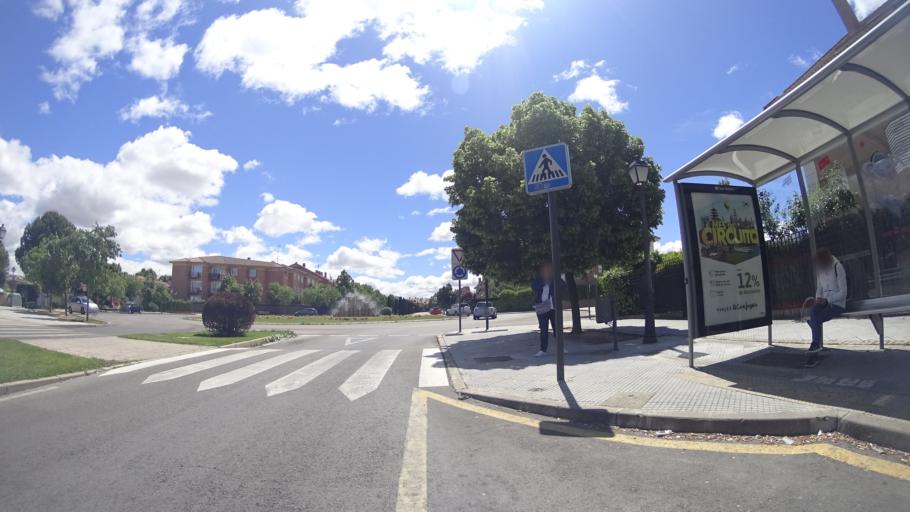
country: ES
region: Madrid
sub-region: Provincia de Madrid
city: Villaviciosa de Odon
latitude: 40.3634
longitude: -3.9146
